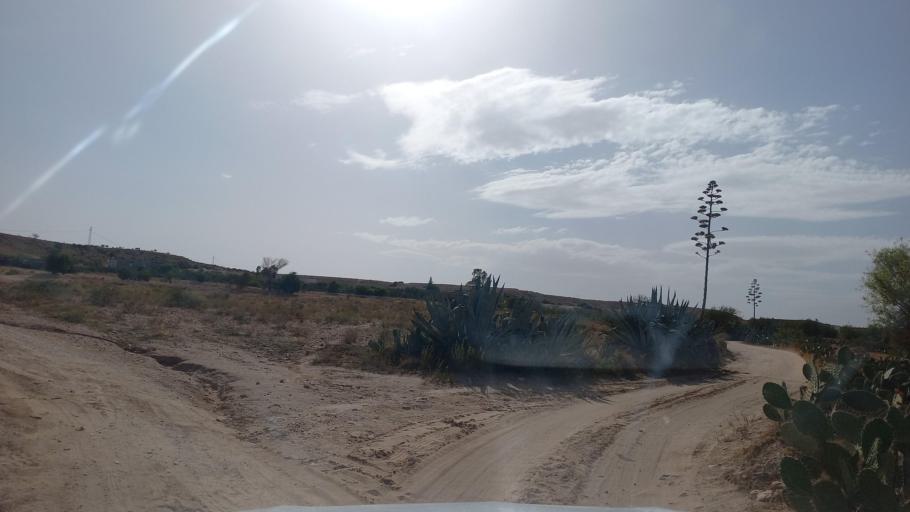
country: TN
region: Al Qasrayn
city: Kasserine
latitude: 35.2631
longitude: 8.9307
